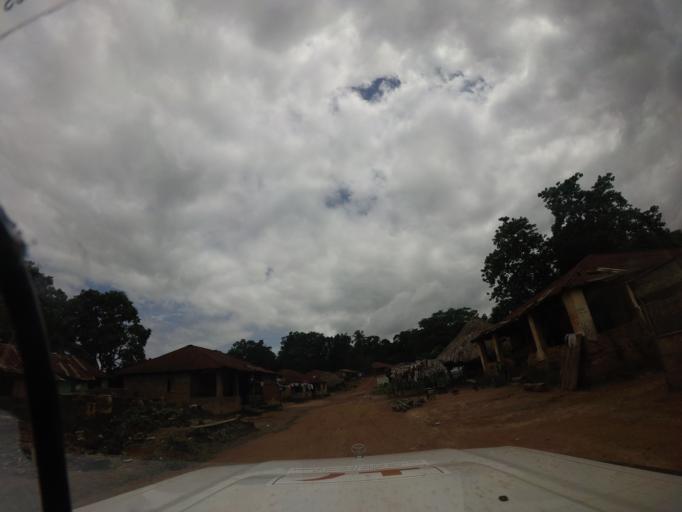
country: SL
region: Northern Province
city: Kamakwie
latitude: 9.5901
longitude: -12.2181
